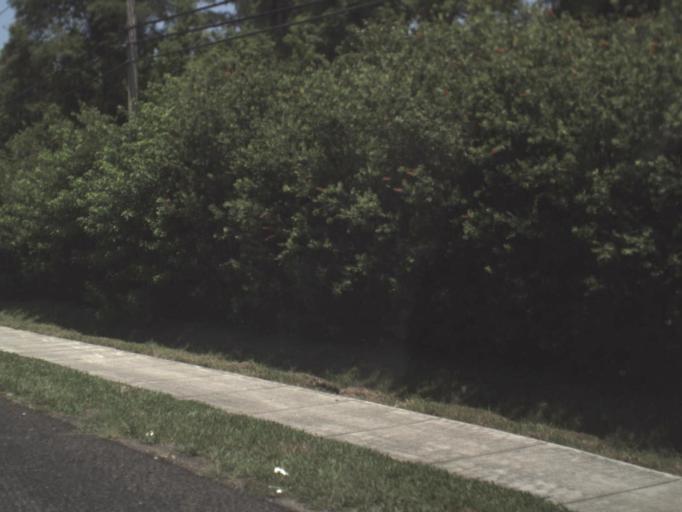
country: US
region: Florida
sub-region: Pinellas County
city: Tarpon Springs
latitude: 28.1177
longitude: -82.7398
